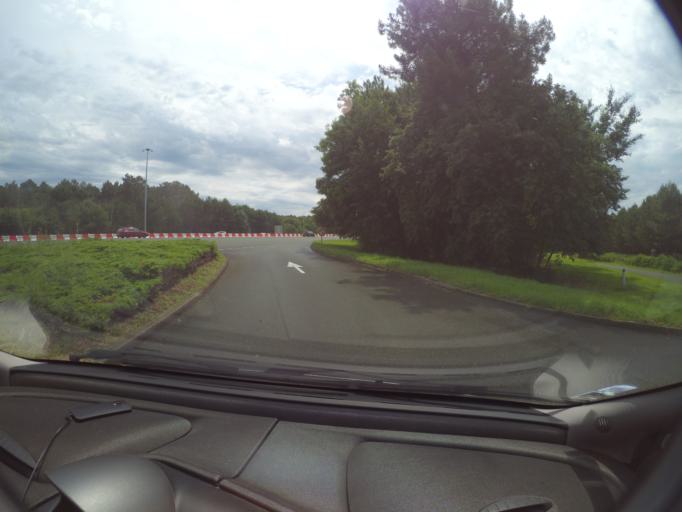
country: FR
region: Pays de la Loire
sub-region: Departement de Maine-et-Loire
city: Seiches-sur-le-Loir
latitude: 47.5376
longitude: -0.3424
